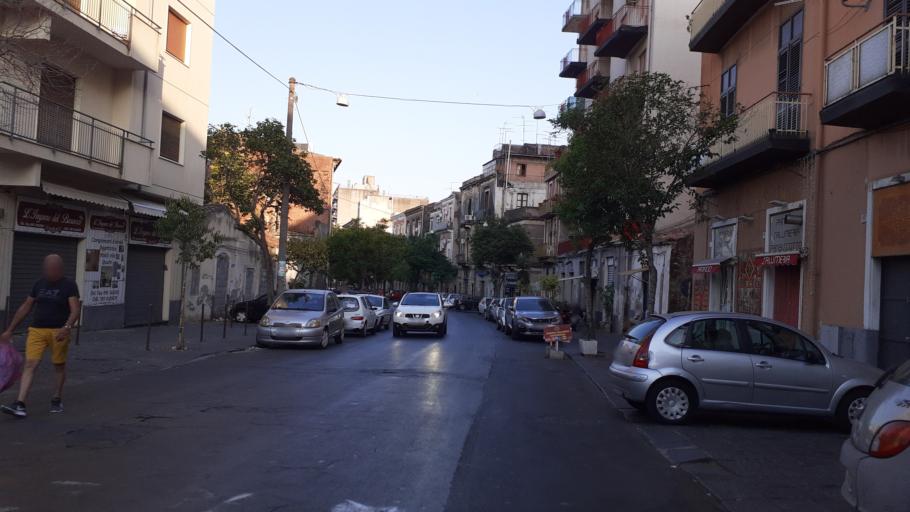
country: IT
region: Sicily
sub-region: Catania
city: Catania
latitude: 37.4993
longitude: 15.0772
